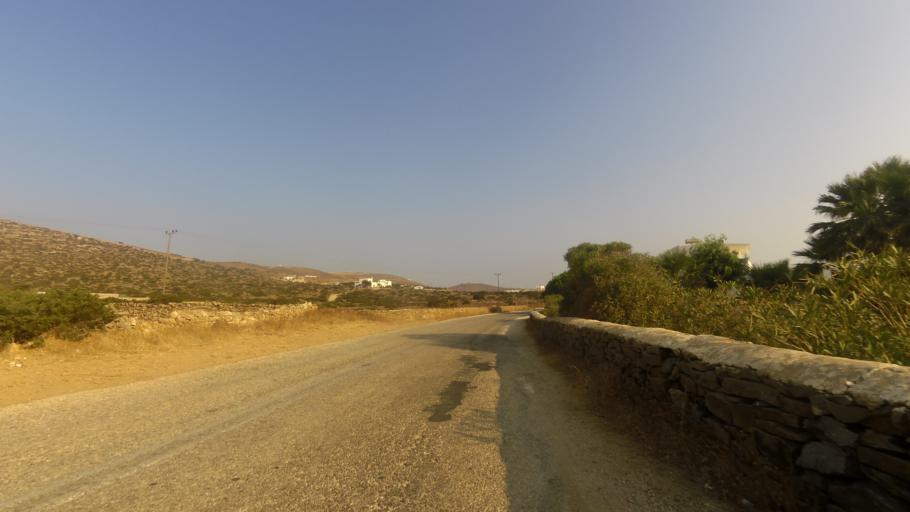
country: GR
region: South Aegean
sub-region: Nomos Kykladon
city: Antiparos
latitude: 37.0235
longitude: 25.0767
